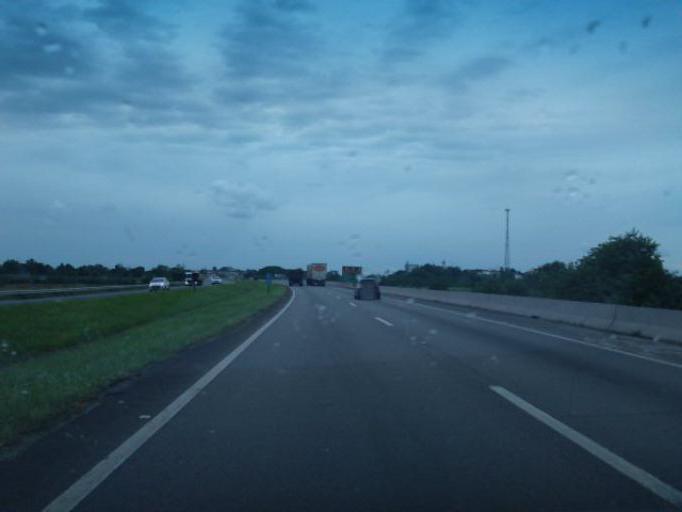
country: BR
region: Sao Paulo
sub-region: Registro
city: Registro
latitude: -24.4825
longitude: -47.8322
